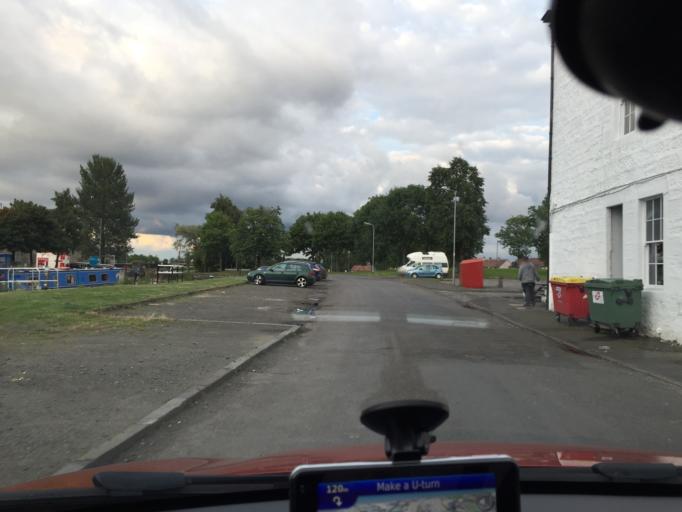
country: GB
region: Scotland
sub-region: Falkirk
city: Larbert
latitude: 55.9996
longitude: -3.8175
